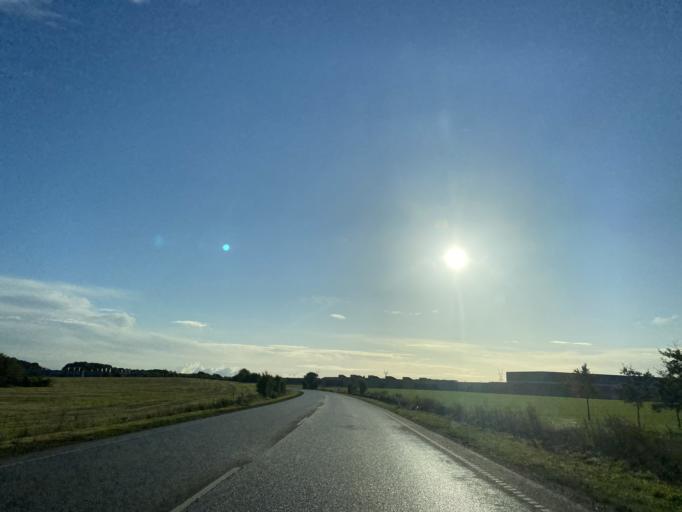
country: DK
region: Central Jutland
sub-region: Horsens Kommune
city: Horsens
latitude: 55.8895
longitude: 9.7683
